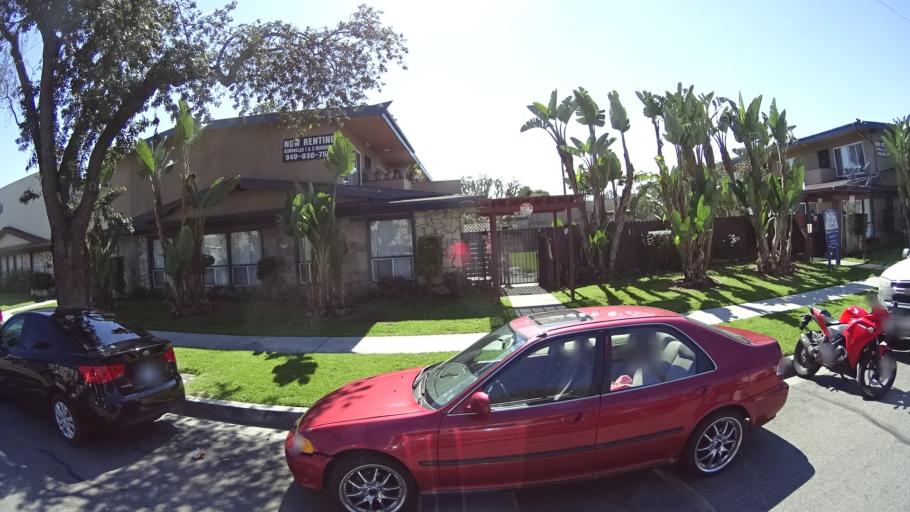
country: US
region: California
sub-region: Orange County
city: Garden Grove
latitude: 33.8054
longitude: -117.9469
